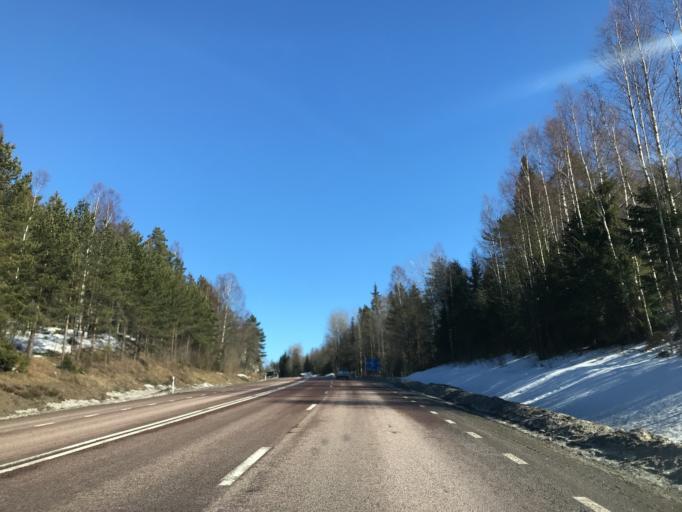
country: SE
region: Vaermland
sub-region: Filipstads Kommun
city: Filipstad
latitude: 59.7152
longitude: 14.1958
